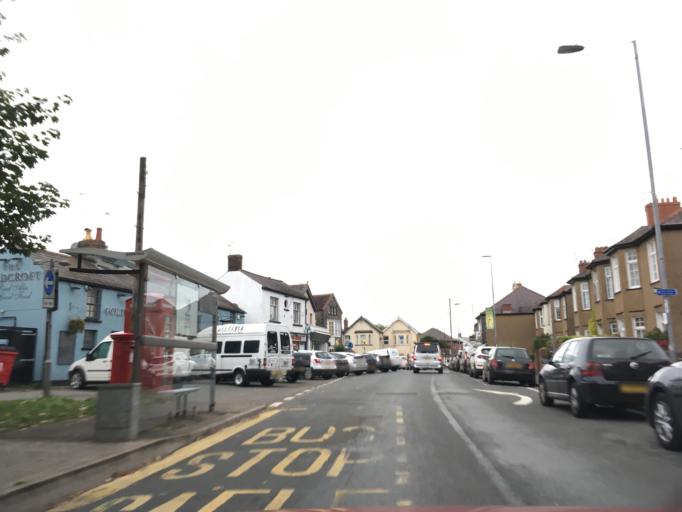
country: GB
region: Wales
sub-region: Newport
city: Caerleon
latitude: 51.6127
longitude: -2.9567
